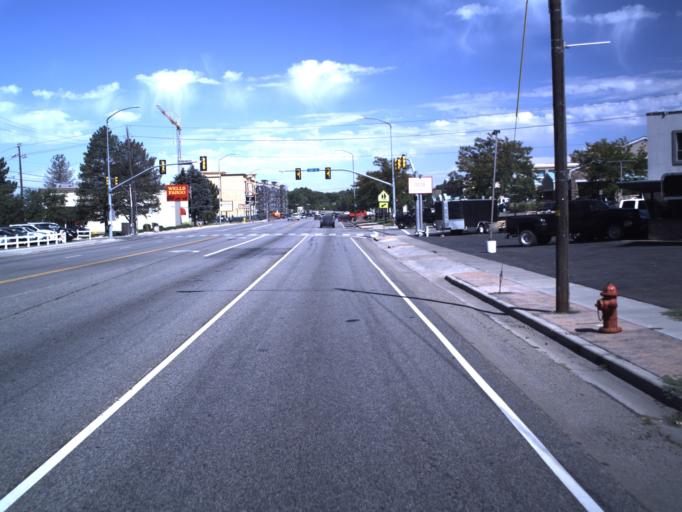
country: US
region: Utah
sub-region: Davis County
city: Clearfield
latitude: 41.1102
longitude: -112.0226
